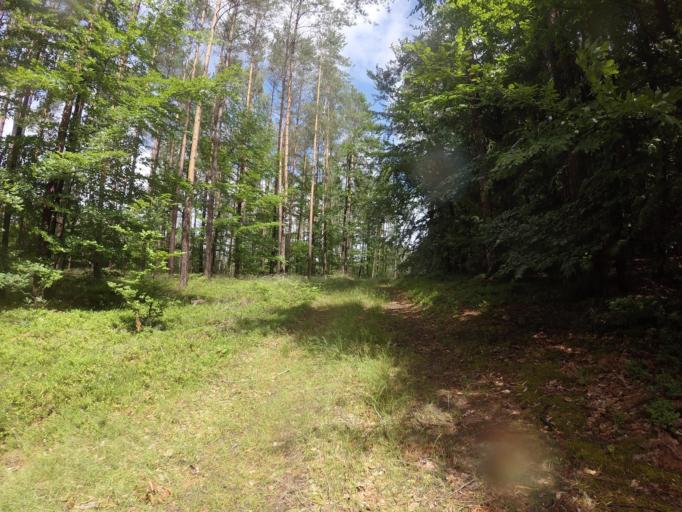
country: PL
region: West Pomeranian Voivodeship
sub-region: Powiat choszczenski
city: Bierzwnik
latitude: 53.0135
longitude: 15.5955
